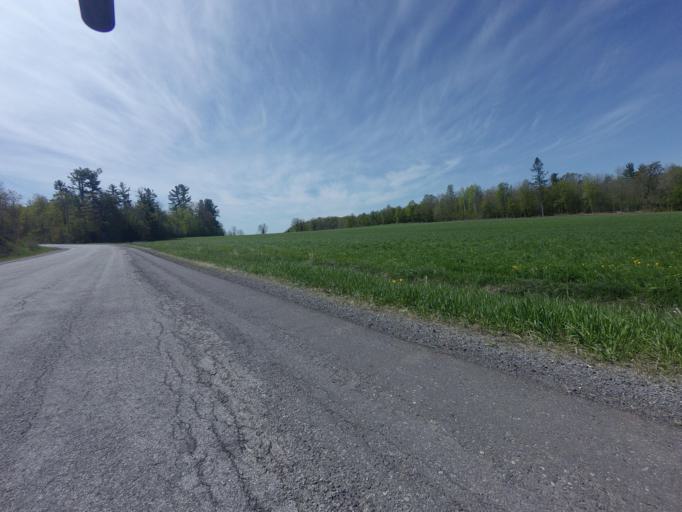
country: CA
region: Ontario
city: Arnprior
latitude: 45.4053
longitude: -76.2071
